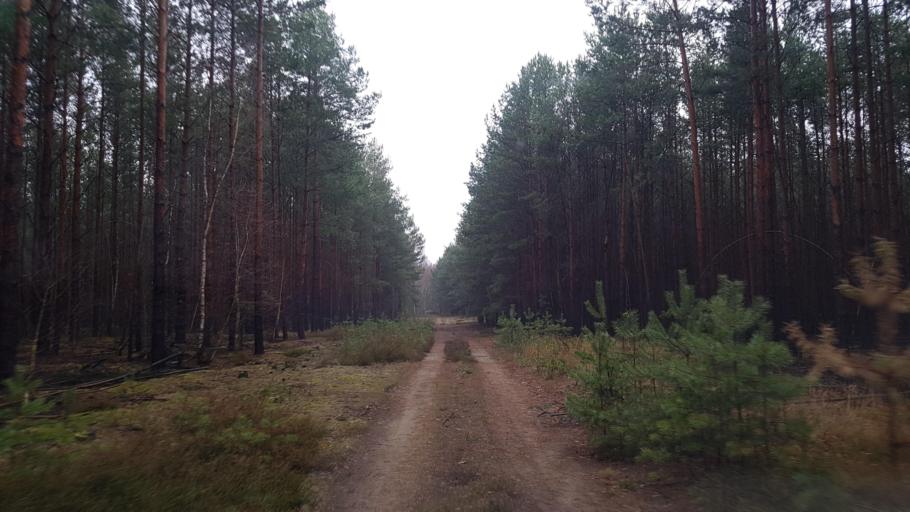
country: DE
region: Brandenburg
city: Grossraschen
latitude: 51.6271
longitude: 13.9686
